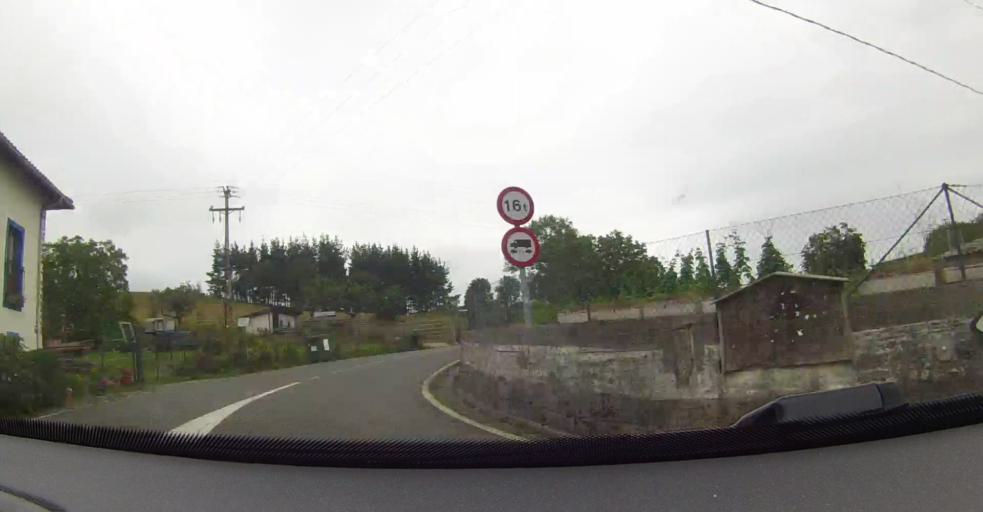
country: ES
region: Basque Country
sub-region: Bizkaia
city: Balmaseda
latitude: 43.2268
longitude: -3.1904
